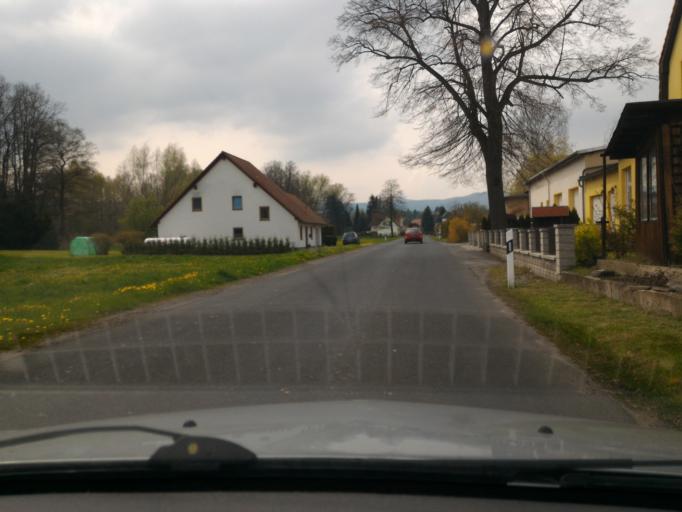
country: DE
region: Saxony
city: Grossschonau
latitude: 50.8968
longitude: 14.6898
